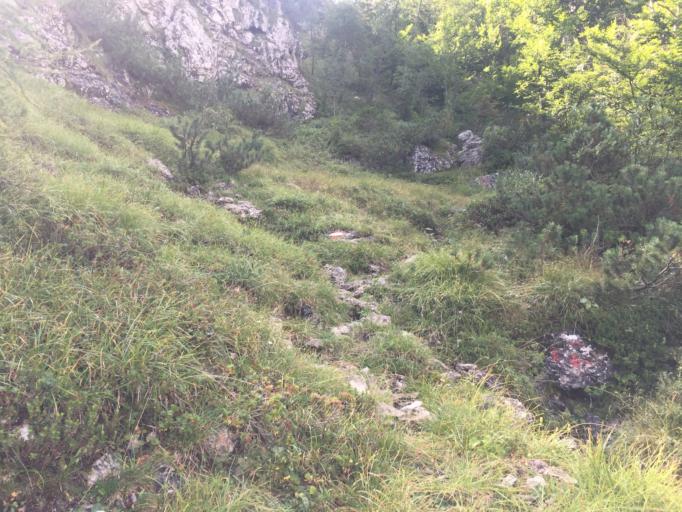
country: IT
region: Friuli Venezia Giulia
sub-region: Provincia di Pordenone
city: Tramonti di Sopra
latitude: 46.3209
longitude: 12.7307
